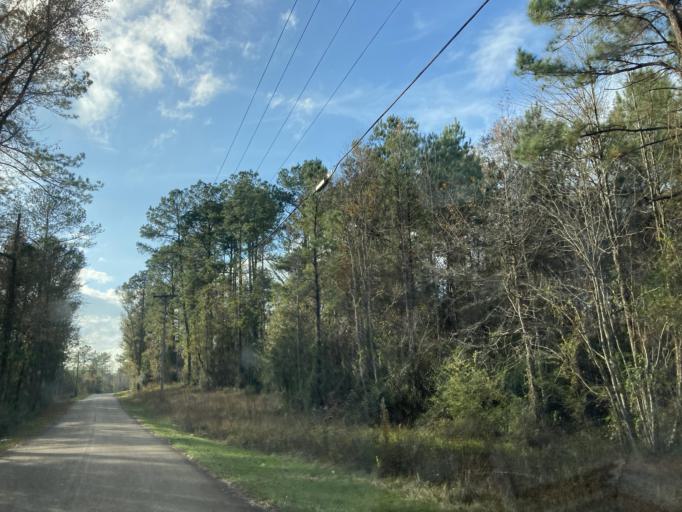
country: US
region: Mississippi
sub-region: Lamar County
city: Purvis
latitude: 31.1420
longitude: -89.6319
